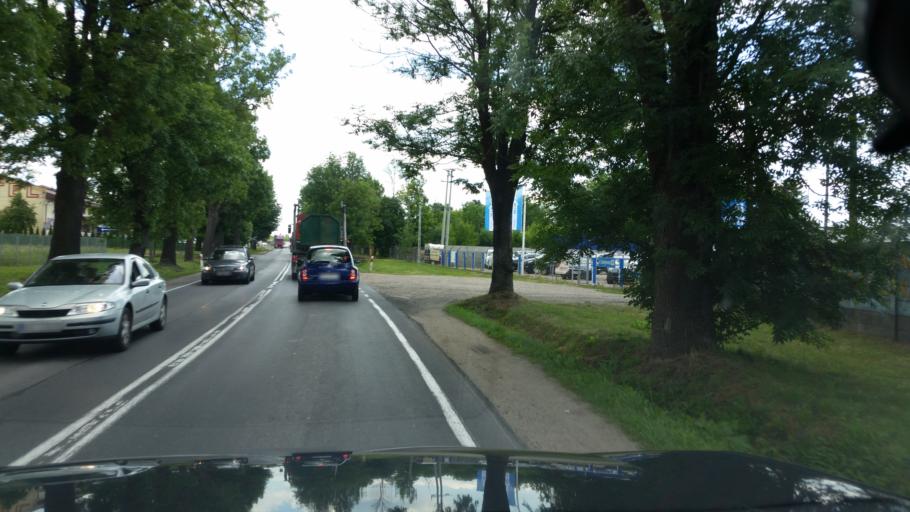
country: PL
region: Masovian Voivodeship
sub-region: Powiat ostrowski
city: Ostrow Mazowiecka
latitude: 52.8283
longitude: 21.8785
